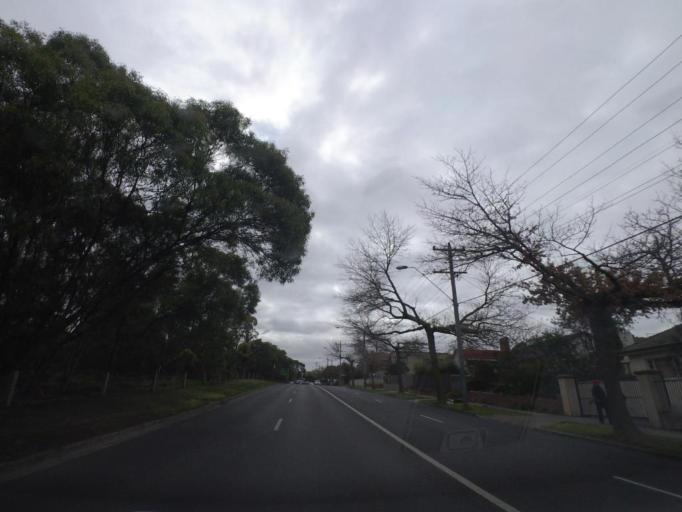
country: AU
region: Victoria
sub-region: Whitehorse
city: Burwood
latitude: -37.8404
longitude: 145.1106
